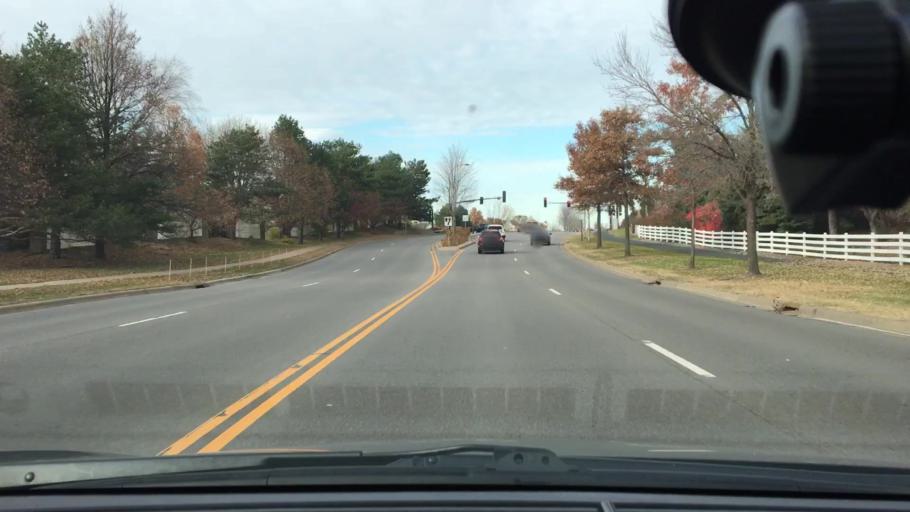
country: US
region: Minnesota
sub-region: Hennepin County
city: Maple Grove
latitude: 45.1150
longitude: -93.4923
